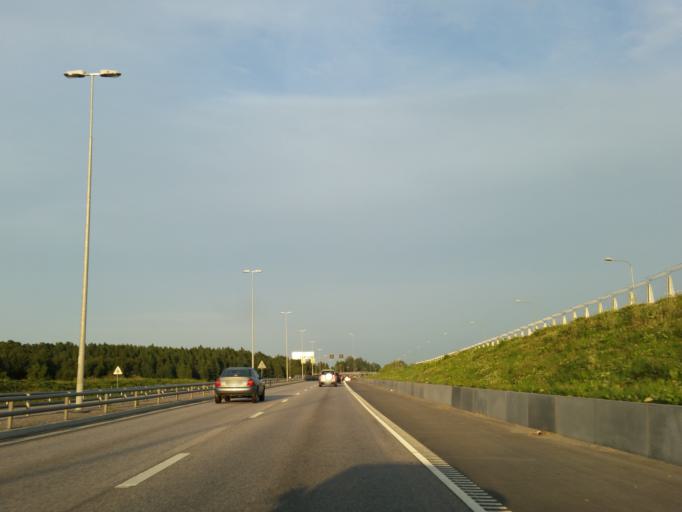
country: SE
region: Stockholm
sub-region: Stockholms Kommun
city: Kista
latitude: 59.3989
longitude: 17.9017
